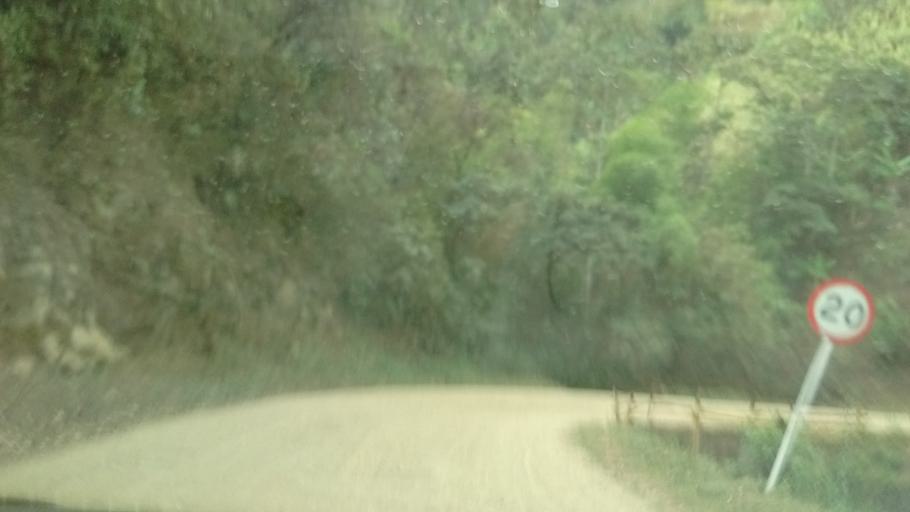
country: CO
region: Cauca
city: La Vega
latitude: 2.0516
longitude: -76.8044
